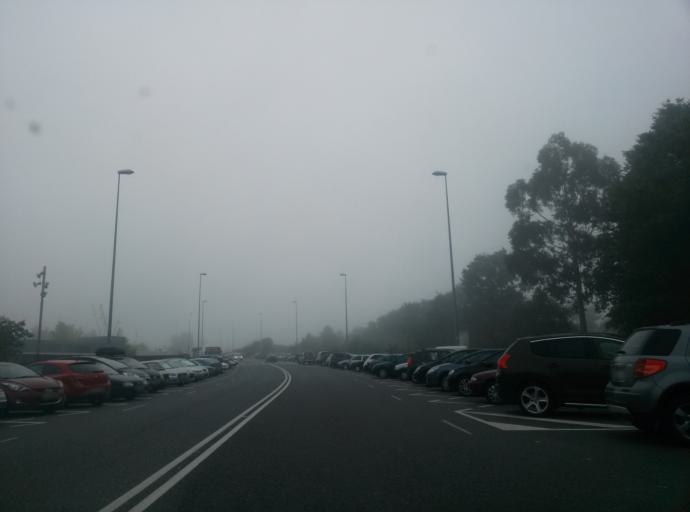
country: ES
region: Galicia
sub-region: Provincia de Lugo
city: Lugo
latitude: 43.0189
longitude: -7.5345
